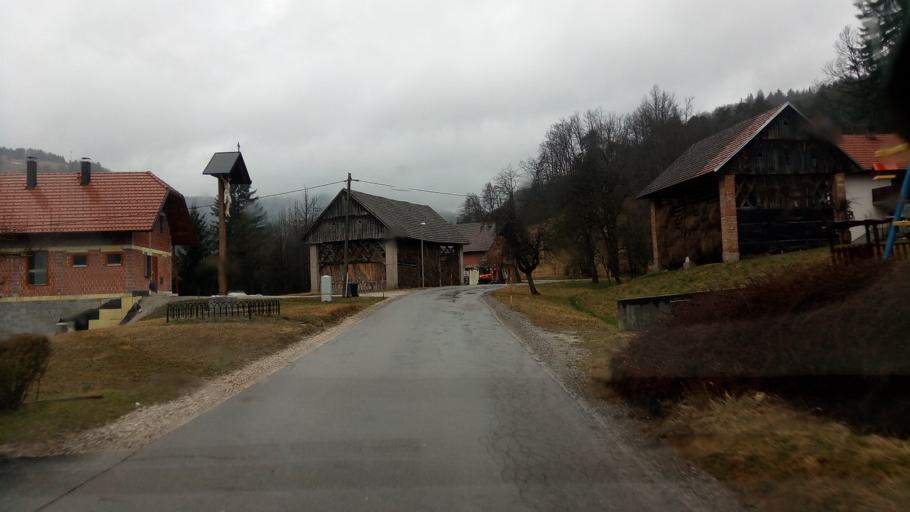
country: SI
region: Horjul
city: Horjul
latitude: 46.0031
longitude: 14.2265
